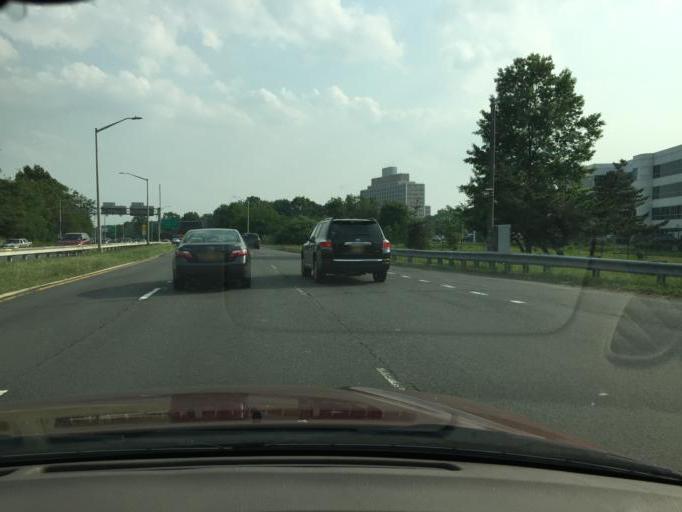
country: US
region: New York
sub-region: Bronx
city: The Bronx
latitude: 40.8530
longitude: -73.8356
